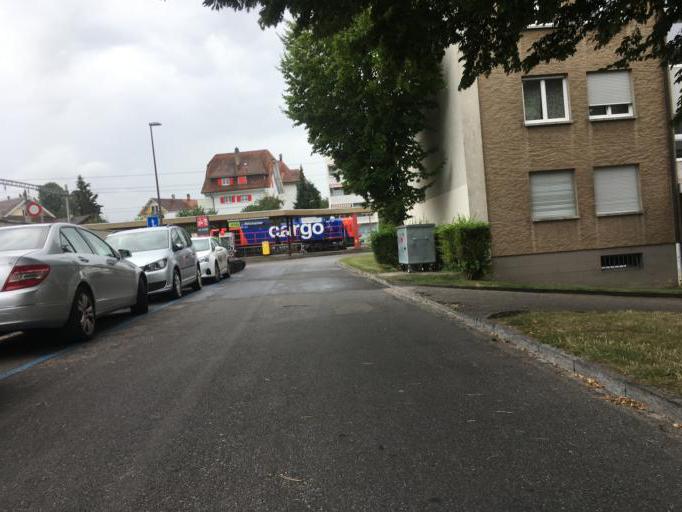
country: CH
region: Bern
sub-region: Bern-Mittelland District
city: Koniz
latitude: 46.9469
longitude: 7.4007
